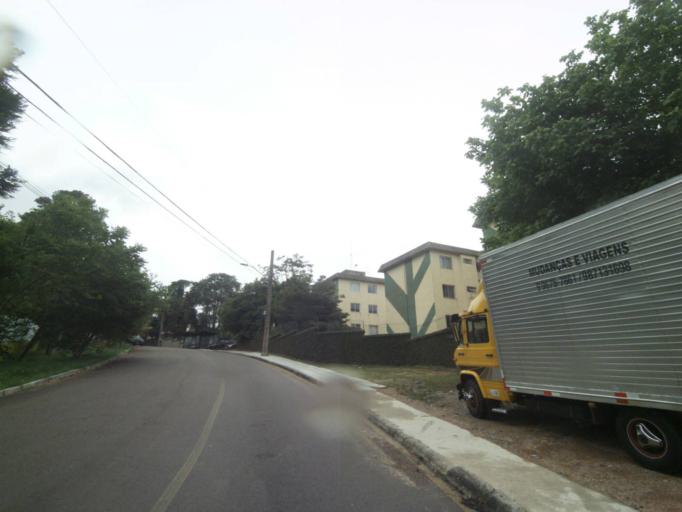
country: BR
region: Parana
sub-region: Curitiba
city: Curitiba
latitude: -25.4621
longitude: -49.3329
